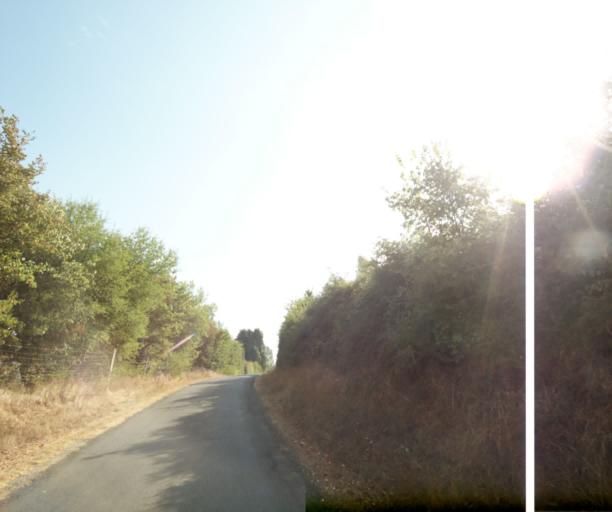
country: FR
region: Poitou-Charentes
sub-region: Departement de la Charente-Maritime
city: Cabariot
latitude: 45.9643
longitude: -0.8573
